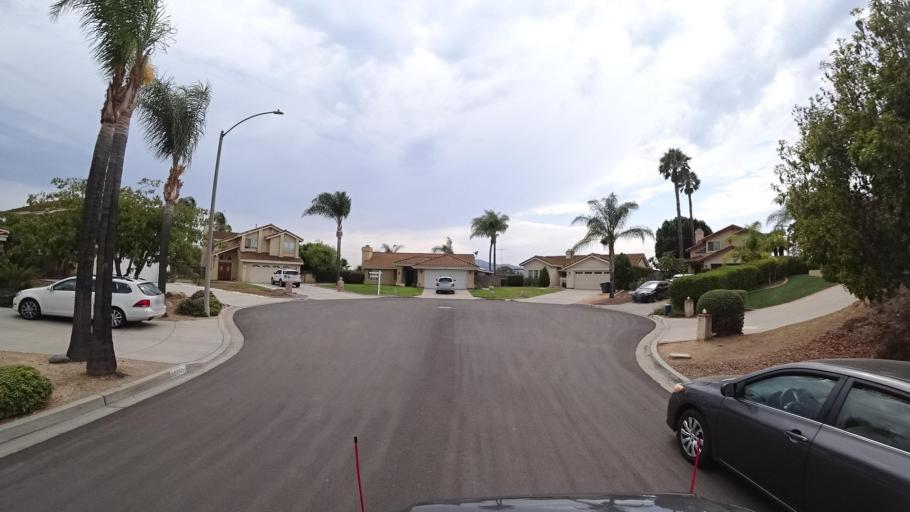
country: US
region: California
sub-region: San Diego County
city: Escondido
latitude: 33.1485
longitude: -117.1171
